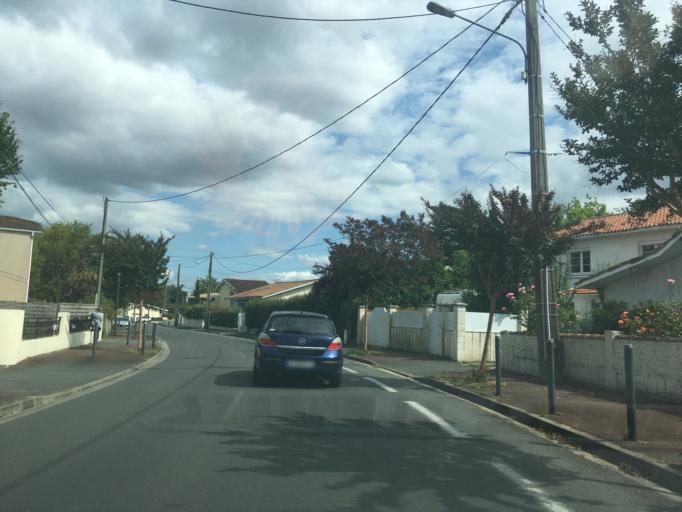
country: FR
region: Aquitaine
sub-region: Departement de la Gironde
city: Merignac
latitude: 44.8482
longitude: -0.6406
